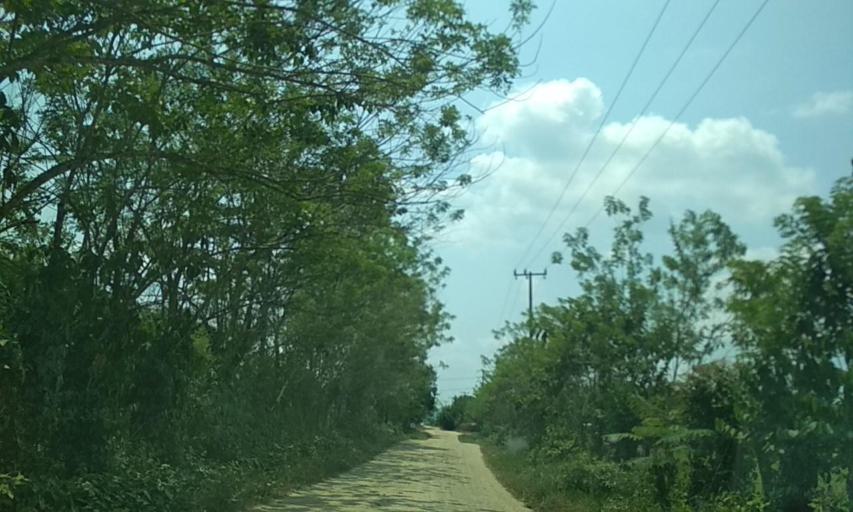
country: MX
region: Chiapas
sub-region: Tecpatan
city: Raudales Malpaso
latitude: 17.3443
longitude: -93.9617
